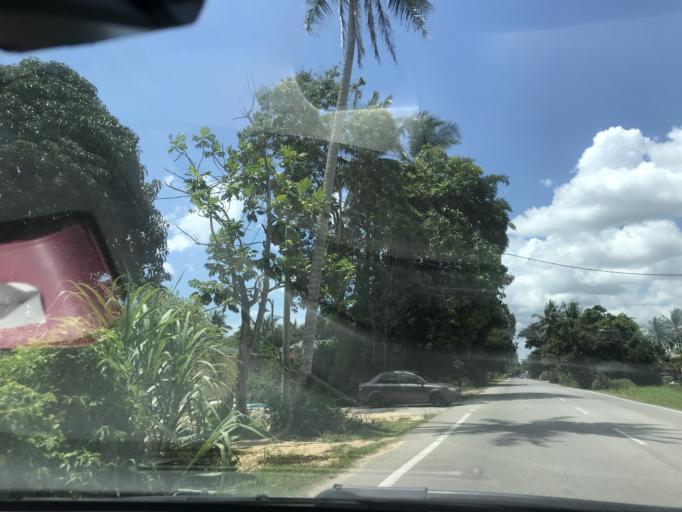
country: MY
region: Kelantan
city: Tumpat
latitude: 6.2000
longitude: 102.1260
